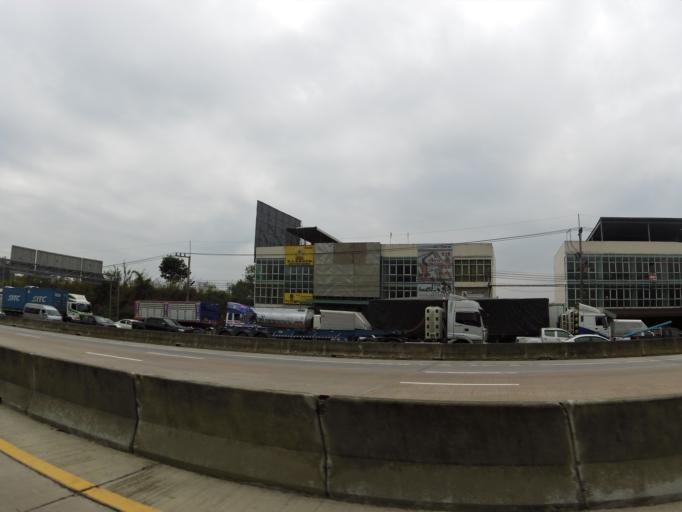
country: TH
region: Chon Buri
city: Ban Talat Bueng
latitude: 13.1116
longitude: 100.9520
